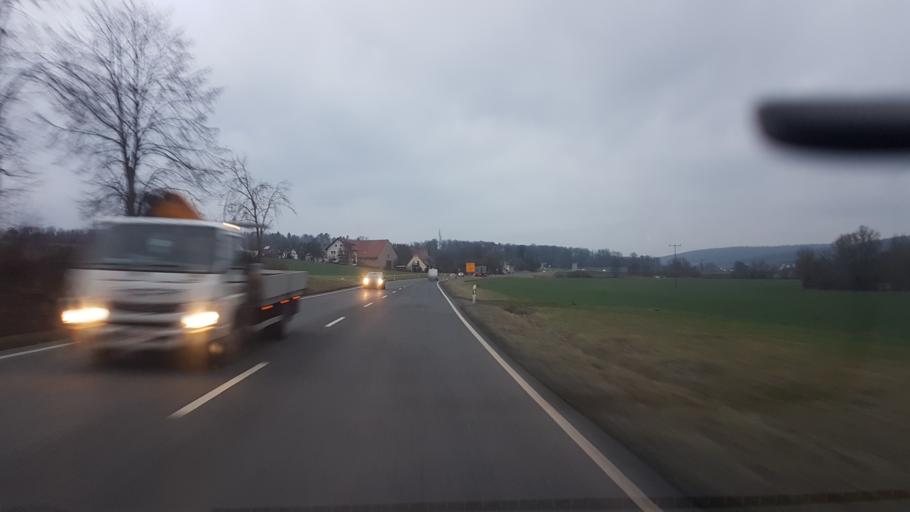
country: DE
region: Bavaria
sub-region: Upper Franconia
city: Gerach
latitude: 50.0436
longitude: 10.8138
